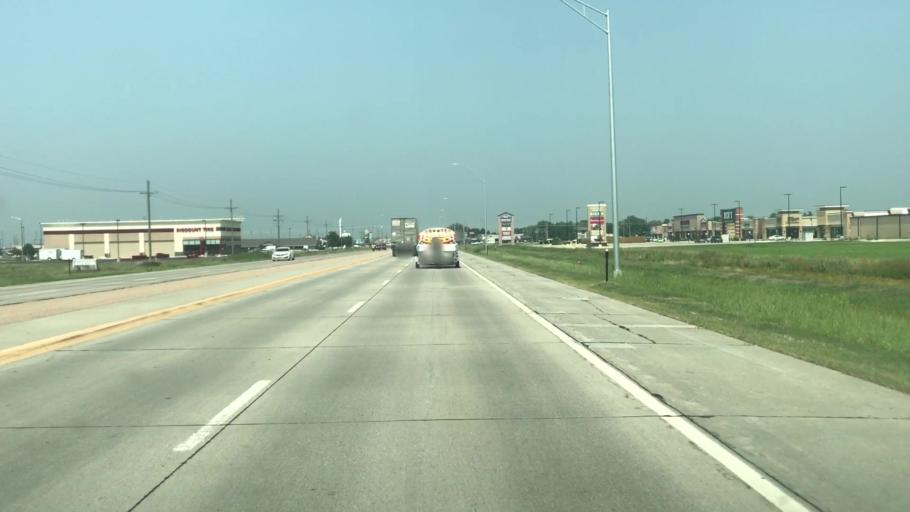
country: US
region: Nebraska
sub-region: Hall County
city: Grand Island
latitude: 40.9409
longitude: -98.3834
